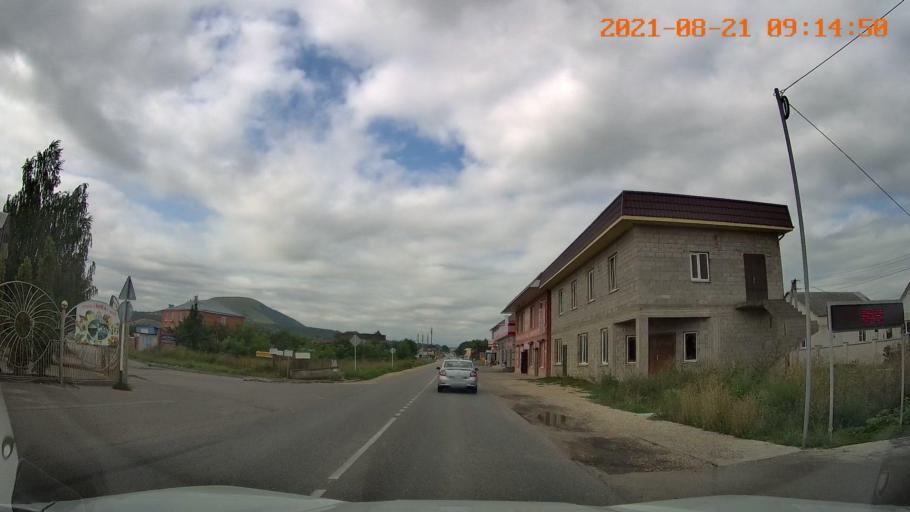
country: RU
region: Stavropol'skiy
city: Svobody
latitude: 43.9967
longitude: 43.0415
